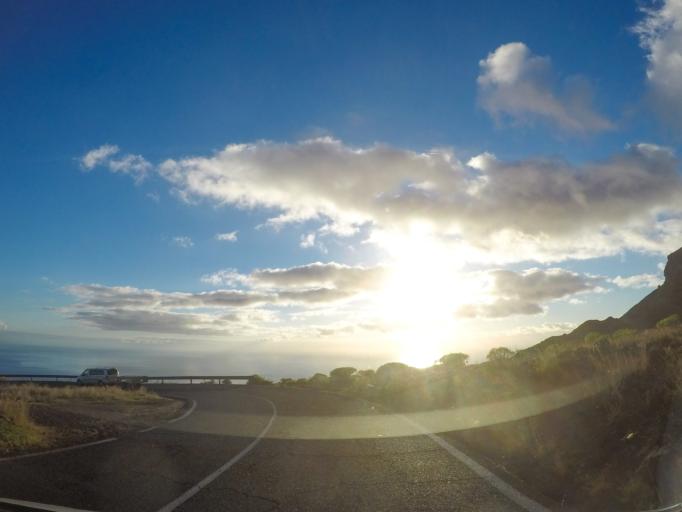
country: ES
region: Canary Islands
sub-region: Provincia de Santa Cruz de Tenerife
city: Alajero
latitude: 28.0514
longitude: -17.2331
